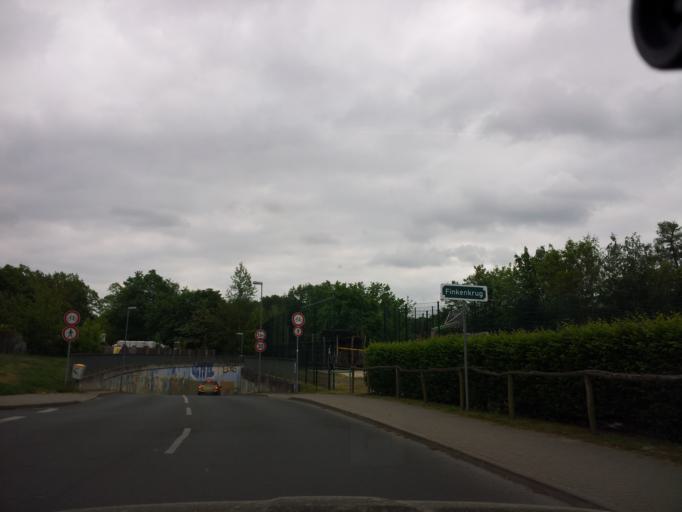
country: DE
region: Brandenburg
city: Dallgow-Doeberitz
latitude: 52.5699
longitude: 13.0530
